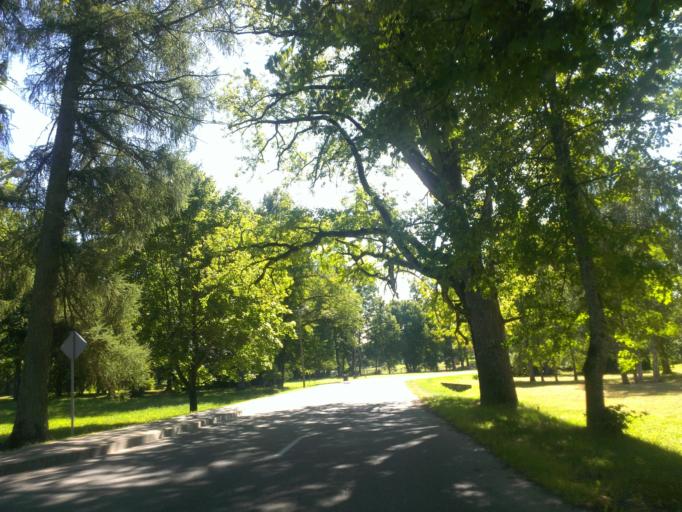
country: LV
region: Malpils
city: Malpils
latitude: 57.0088
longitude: 24.9501
